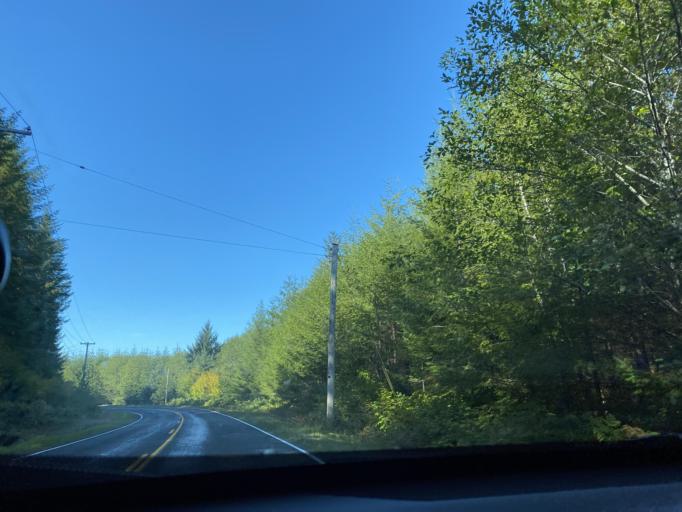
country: US
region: Washington
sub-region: Clallam County
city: Forks
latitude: 47.9508
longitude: -124.4754
